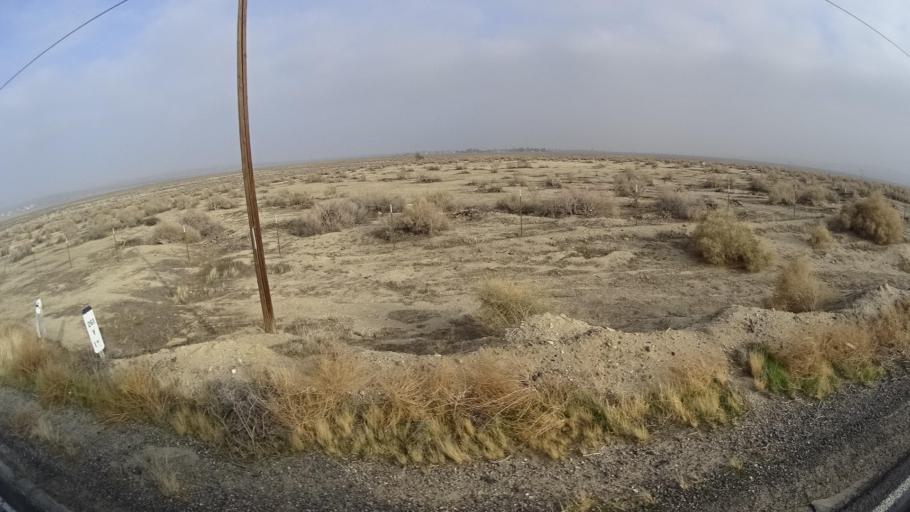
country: US
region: California
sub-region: Kern County
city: Ford City
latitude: 35.2128
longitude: -119.4456
